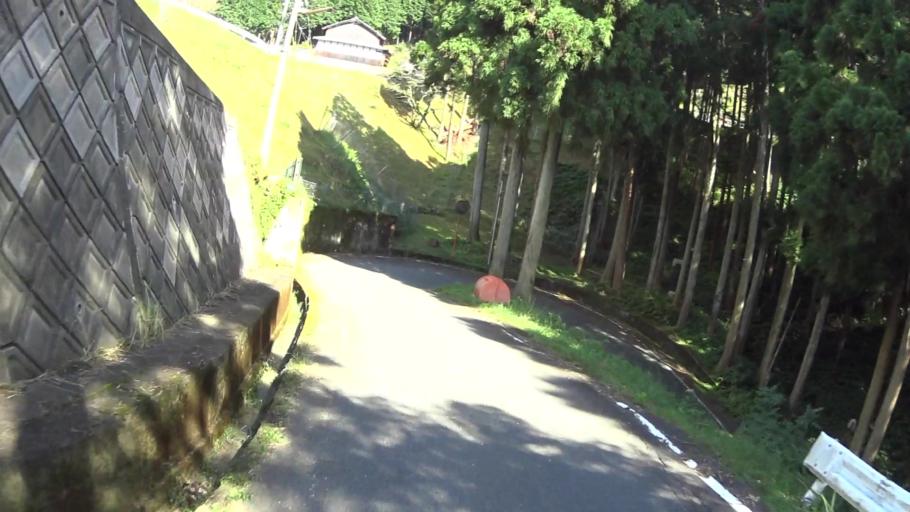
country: JP
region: Shiga Prefecture
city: Otsu-shi
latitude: 34.9381
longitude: 135.8565
